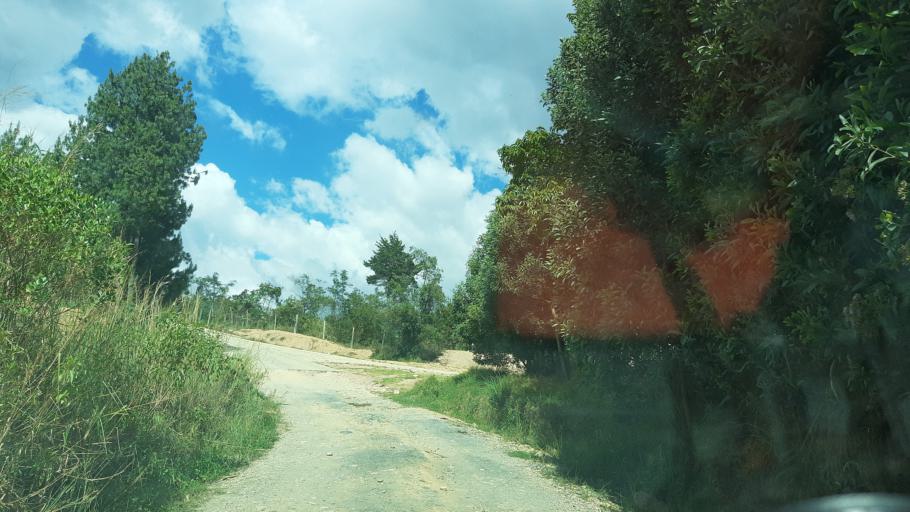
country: CO
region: Boyaca
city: La Capilla
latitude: 5.7103
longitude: -73.5370
